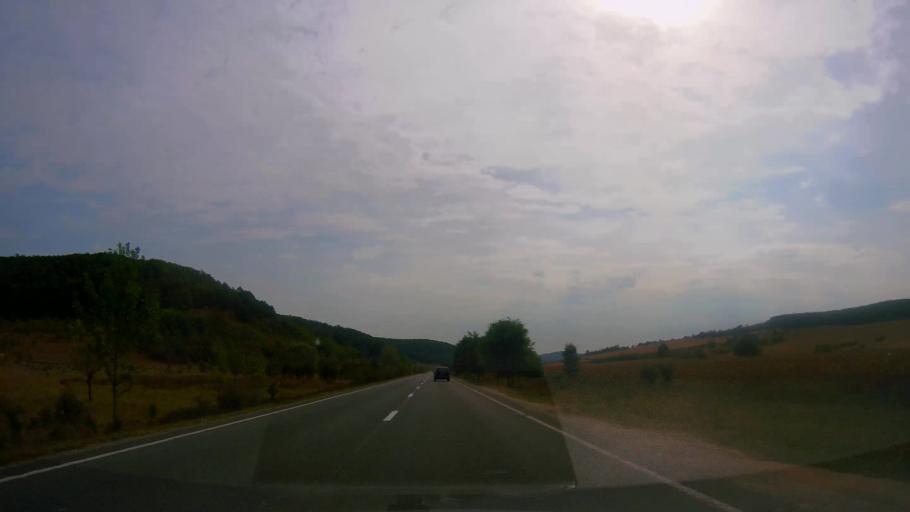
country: RO
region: Salaj
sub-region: Comuna Romanasi
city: Romanasi
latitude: 47.0565
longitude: 23.2238
